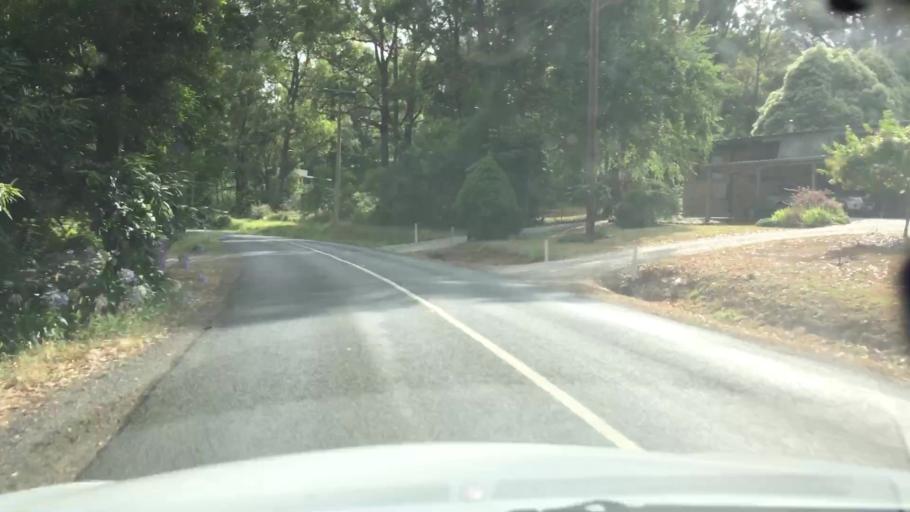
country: AU
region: Victoria
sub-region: Cardinia
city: Emerald
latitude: -37.9201
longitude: 145.4683
